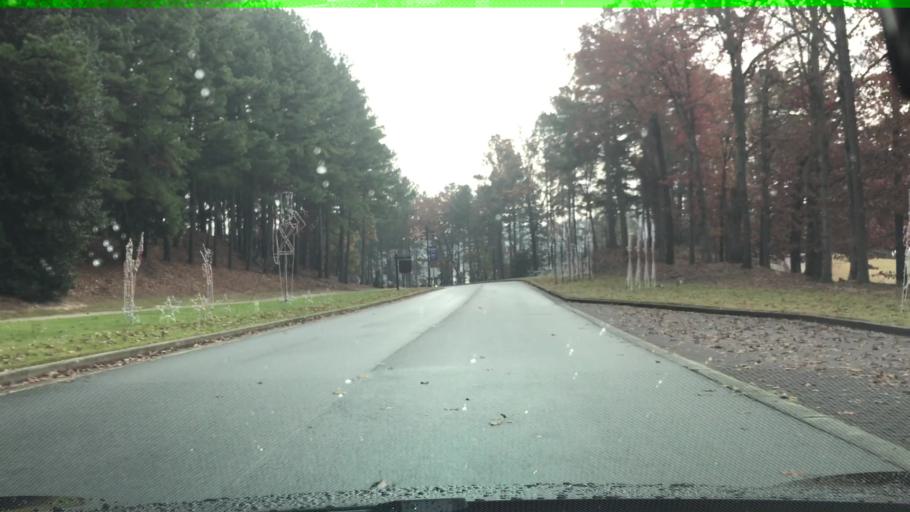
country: US
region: Georgia
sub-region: Gwinnett County
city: Buford
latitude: 34.1752
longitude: -84.0189
